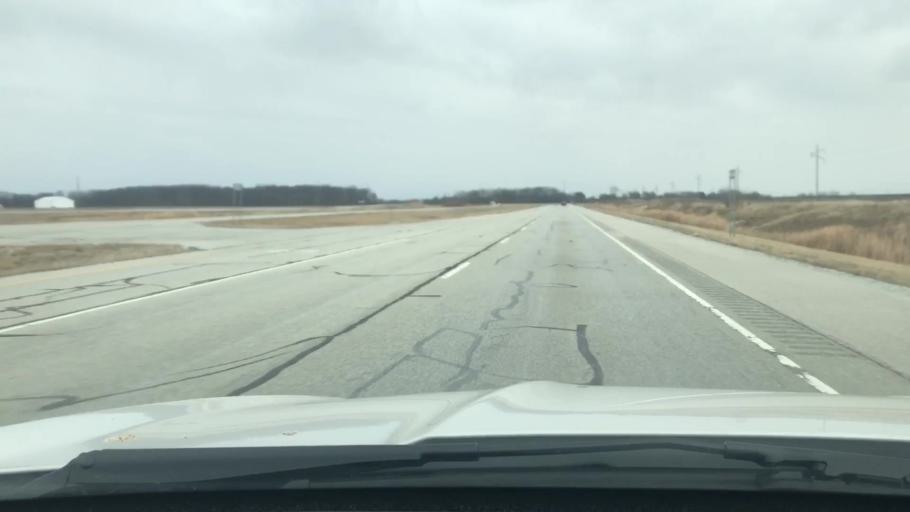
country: US
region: Indiana
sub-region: Carroll County
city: Delphi
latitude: 40.6327
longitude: -86.5920
